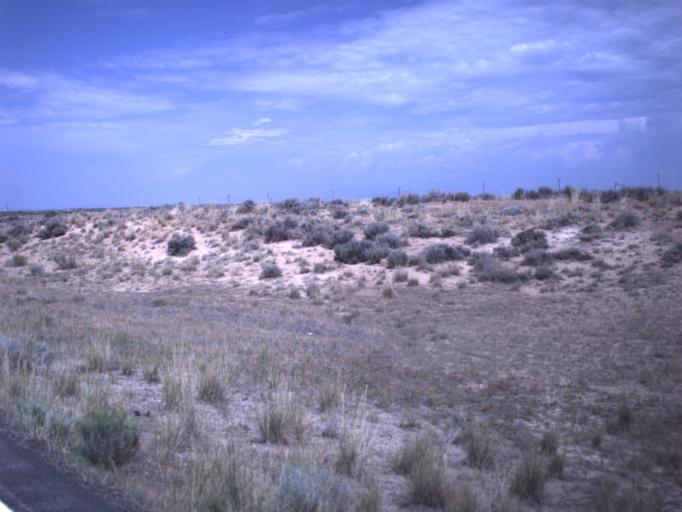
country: US
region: Utah
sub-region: Uintah County
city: Naples
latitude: 40.1996
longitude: -109.3445
